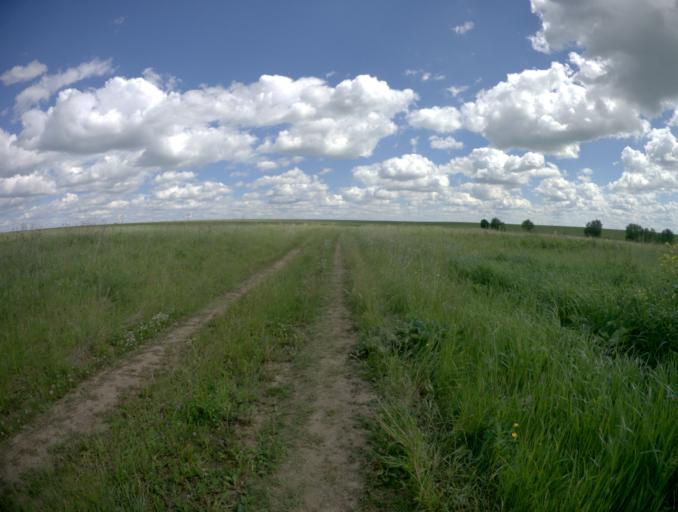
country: RU
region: Ivanovo
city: Gavrilov Posad
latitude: 56.4393
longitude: 40.2572
